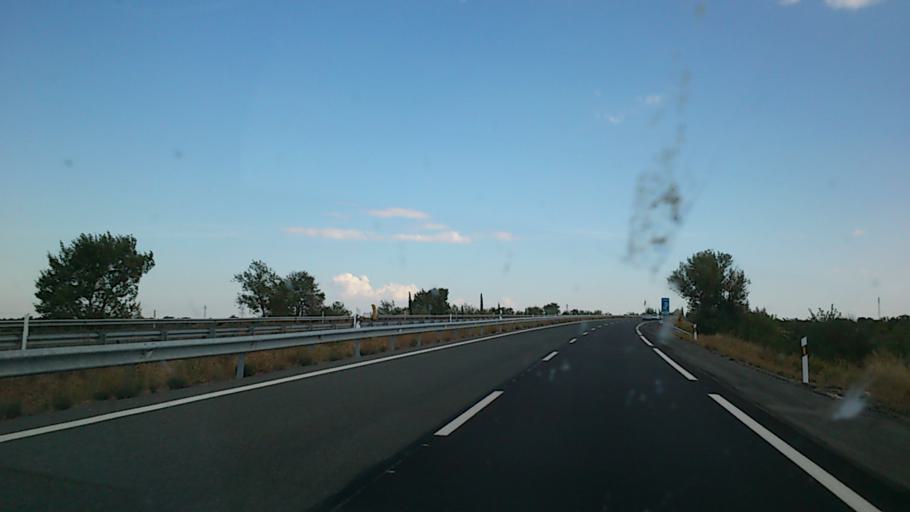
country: ES
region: Navarre
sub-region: Provincia de Navarra
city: Corella
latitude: 42.1229
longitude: -1.7480
